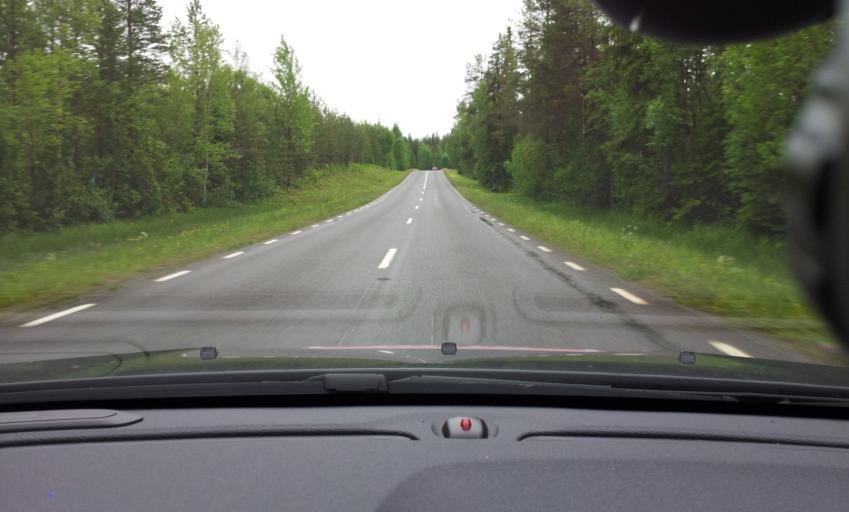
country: SE
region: Jaemtland
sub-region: Stroemsunds Kommun
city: Stroemsund
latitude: 63.4828
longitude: 15.4451
